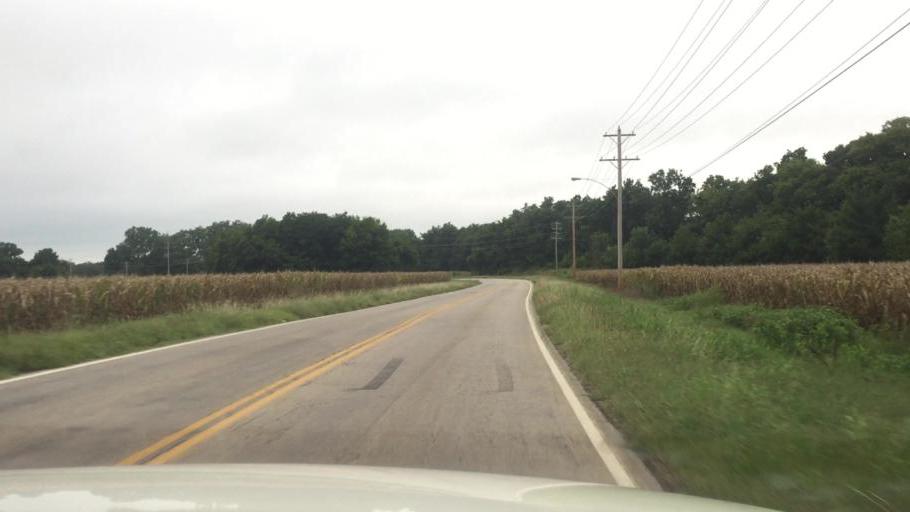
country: US
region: Kansas
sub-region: Montgomery County
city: Coffeyville
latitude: 37.0350
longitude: -95.5818
